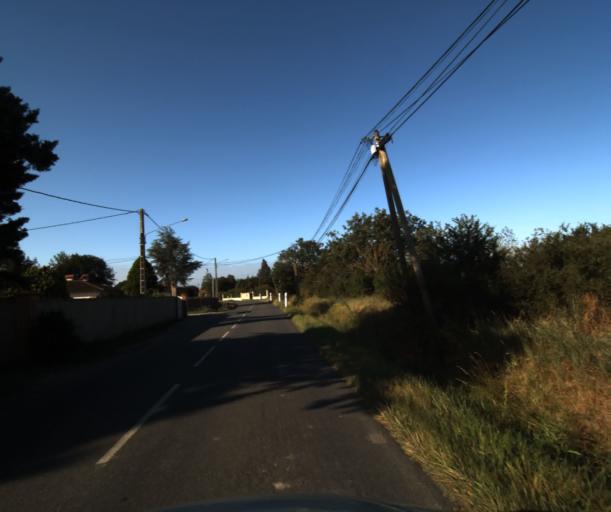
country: FR
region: Midi-Pyrenees
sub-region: Departement de la Haute-Garonne
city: Muret
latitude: 43.4549
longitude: 1.3711
